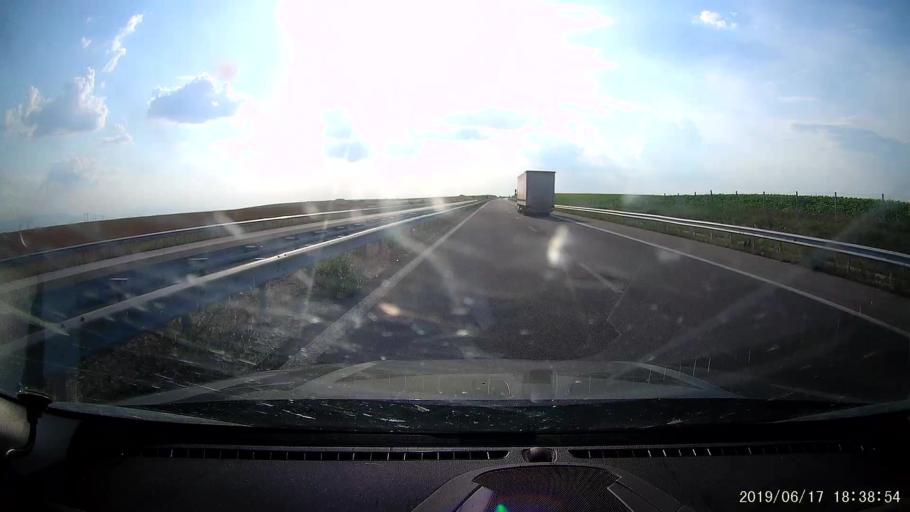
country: BG
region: Stara Zagora
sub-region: Obshtina Chirpan
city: Chirpan
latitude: 42.1402
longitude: 25.3234
